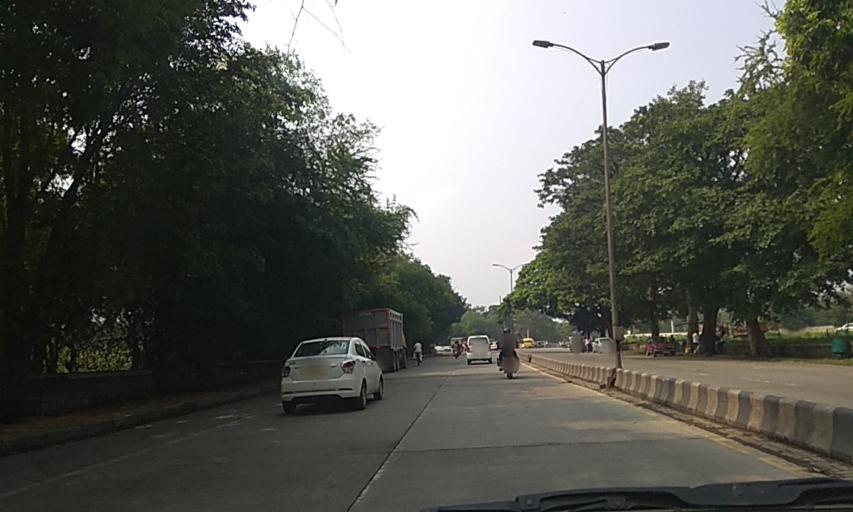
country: IN
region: Maharashtra
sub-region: Pune Division
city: Khadki
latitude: 18.5501
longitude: 73.8521
